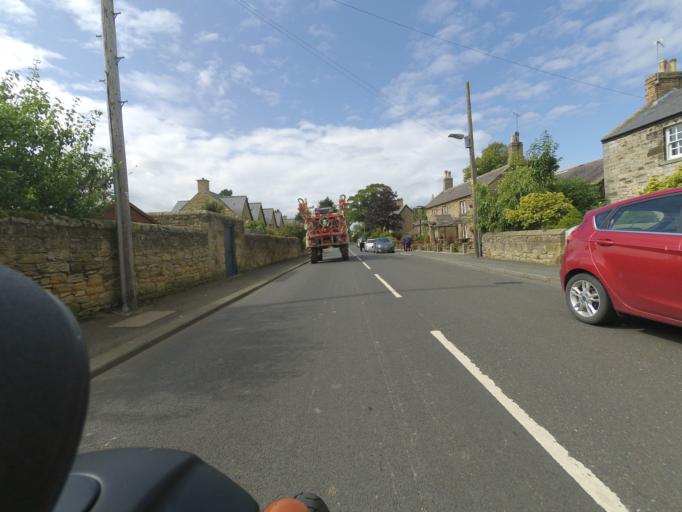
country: GB
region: England
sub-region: Northumberland
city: Alnmouth
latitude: 55.3983
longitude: -1.6295
